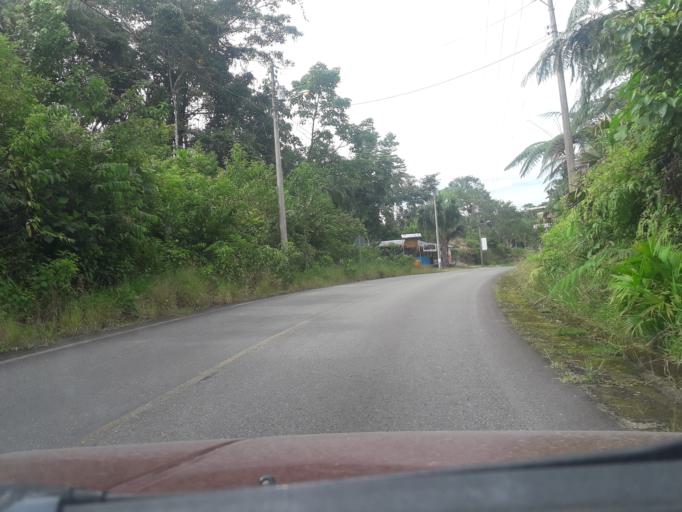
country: EC
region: Napo
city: Tena
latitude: -1.0552
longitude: -77.8955
